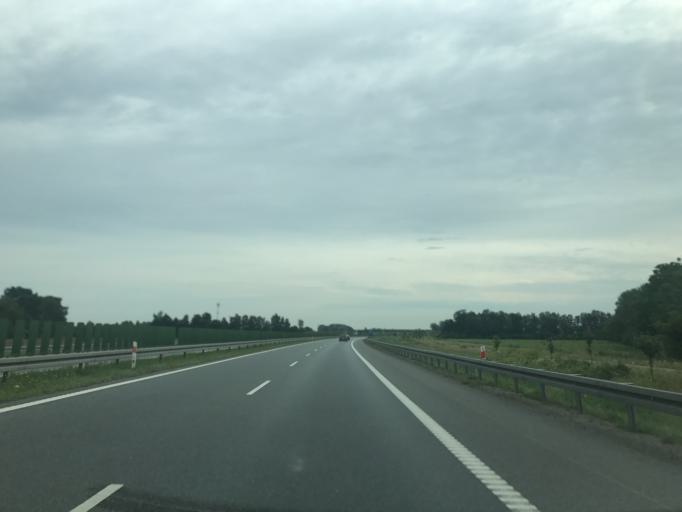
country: PL
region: Pomeranian Voivodeship
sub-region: Gdansk
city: Gdansk
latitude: 54.3213
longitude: 18.7226
